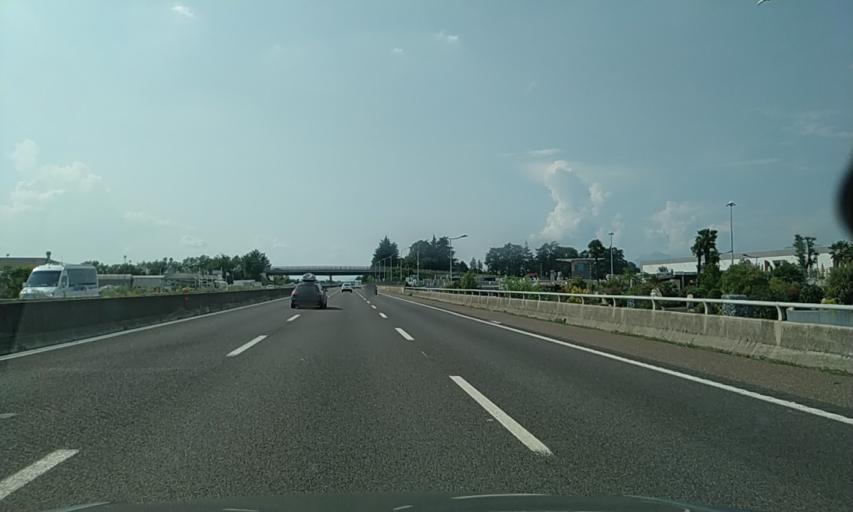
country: IT
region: Lombardy
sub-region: Provincia di Bergamo
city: Bolgare
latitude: 45.6427
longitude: 9.8118
